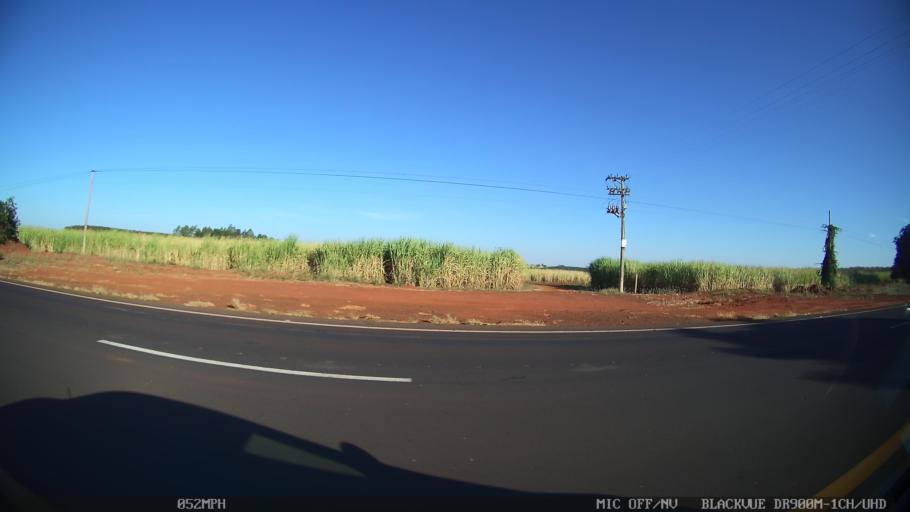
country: BR
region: Sao Paulo
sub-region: Olimpia
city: Olimpia
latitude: -20.7182
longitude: -49.0055
